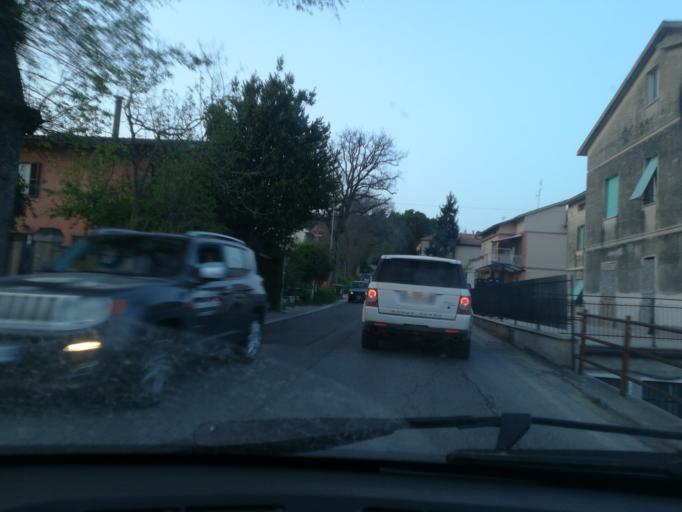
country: IT
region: The Marches
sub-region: Provincia di Macerata
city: Macerata
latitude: 43.2872
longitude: 13.4521
